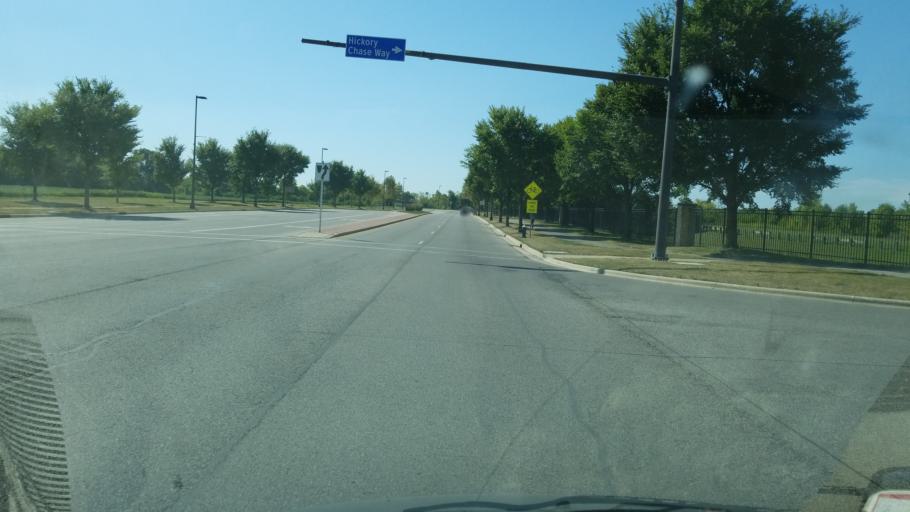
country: US
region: Ohio
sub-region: Franklin County
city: Hilliard
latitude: 40.0451
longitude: -83.1327
